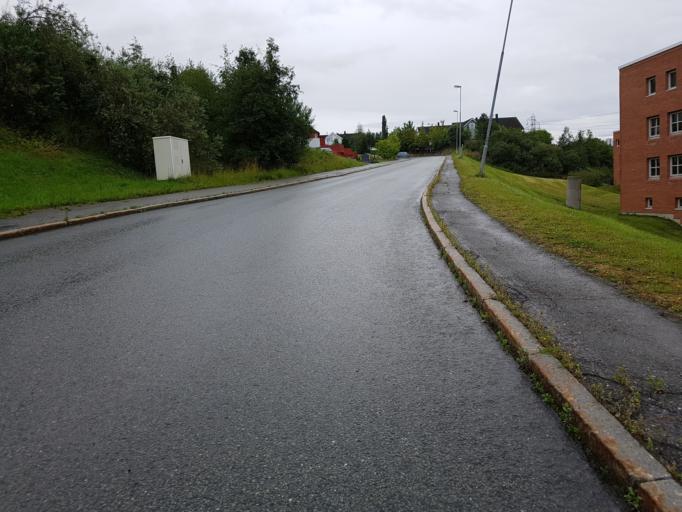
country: NO
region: Sor-Trondelag
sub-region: Trondheim
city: Trondheim
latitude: 63.3986
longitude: 10.4403
